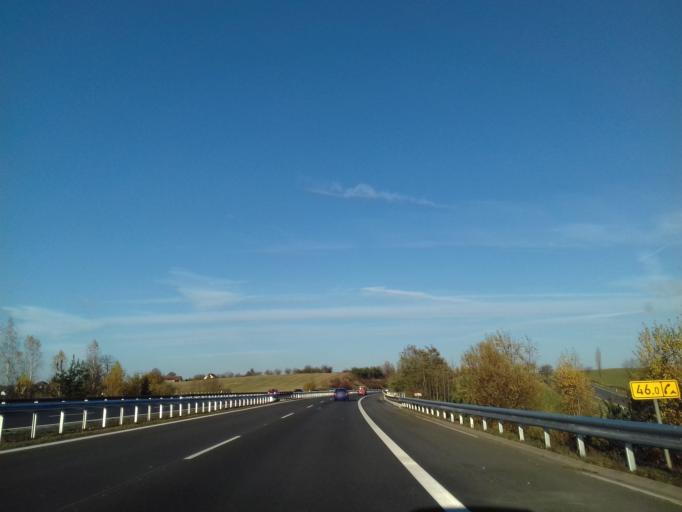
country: CZ
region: Plzensky
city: Myto
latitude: 49.8156
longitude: 13.7618
